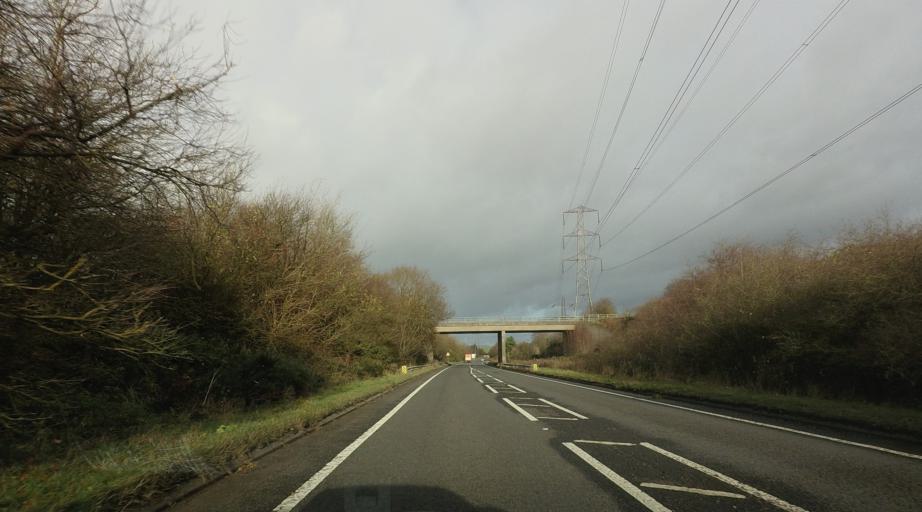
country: GB
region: Scotland
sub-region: West Lothian
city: Armadale
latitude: 55.8954
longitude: -3.6773
